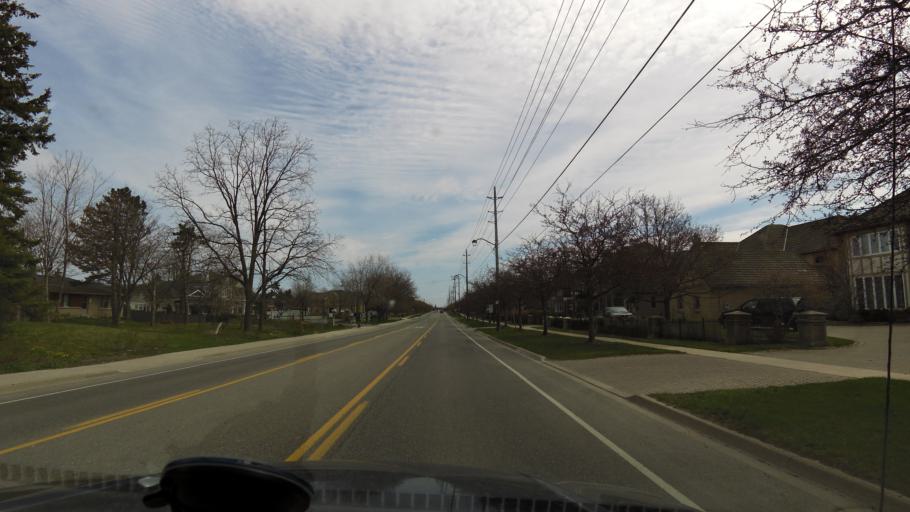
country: CA
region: Ontario
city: Mississauga
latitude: 43.5721
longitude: -79.7008
